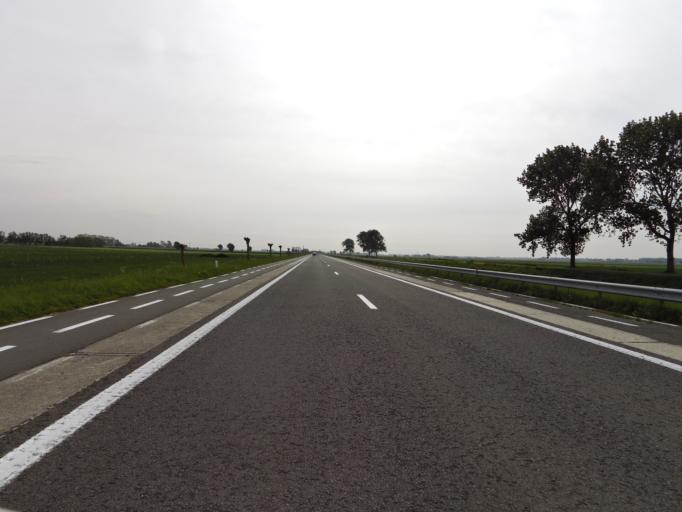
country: BE
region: Flanders
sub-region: Provincie West-Vlaanderen
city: Nieuwpoort
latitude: 51.1179
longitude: 2.7407
